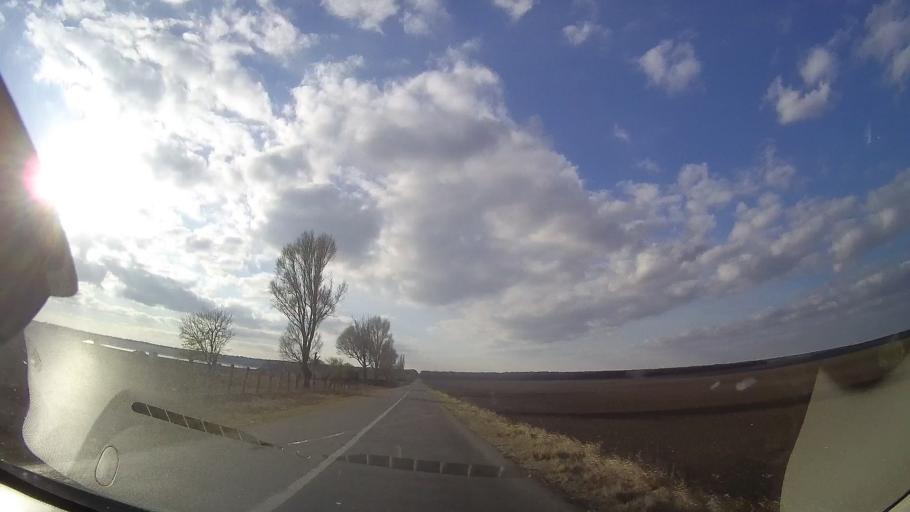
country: RO
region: Constanta
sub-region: Comuna Comana
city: Comana
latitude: 43.8193
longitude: 28.2934
